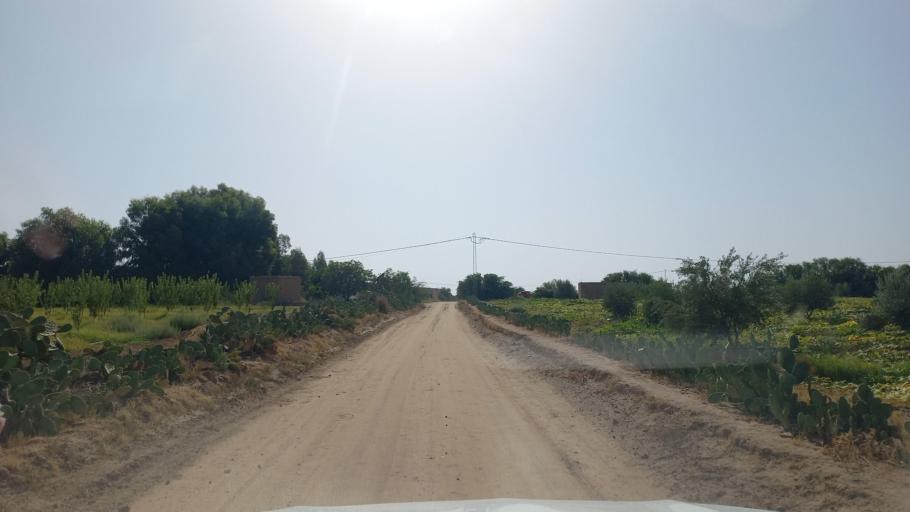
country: TN
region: Al Qasrayn
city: Kasserine
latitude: 35.2457
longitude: 9.0410
